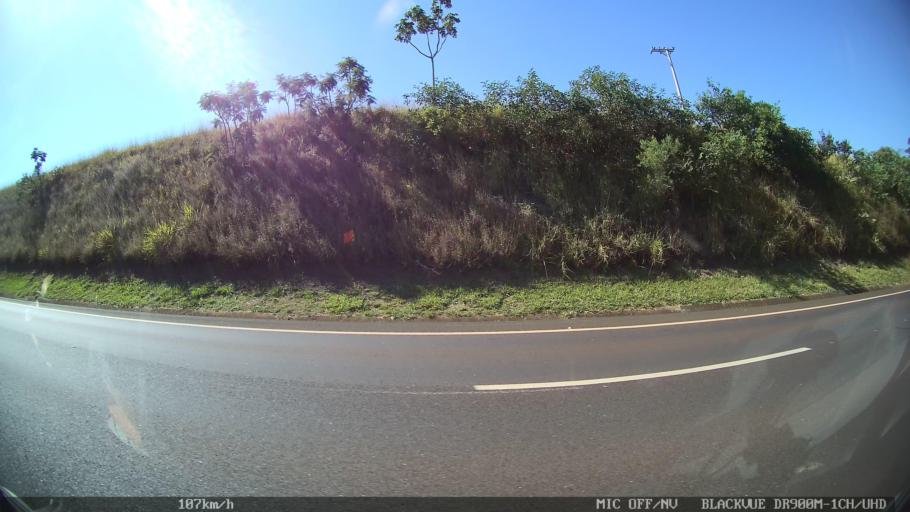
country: BR
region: Sao Paulo
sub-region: Batatais
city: Batatais
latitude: -20.8422
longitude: -47.6014
